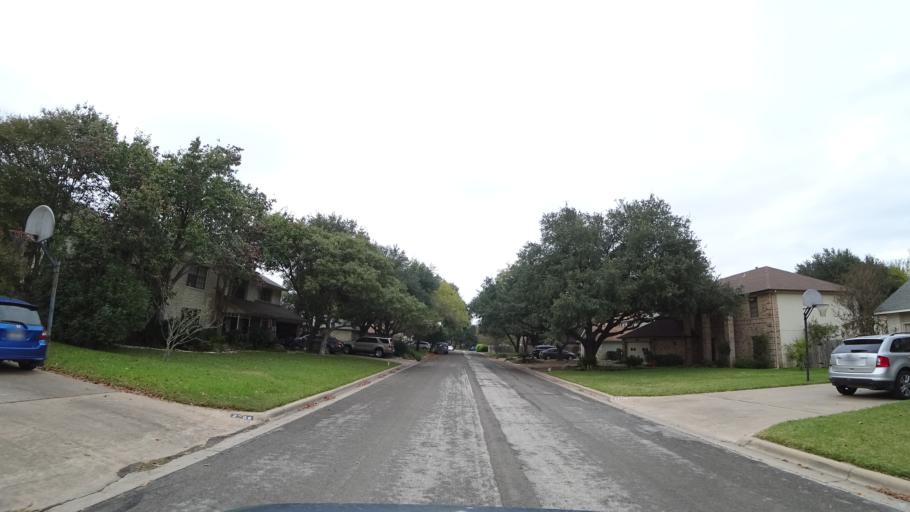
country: US
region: Texas
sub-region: Williamson County
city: Round Rock
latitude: 30.4838
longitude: -97.7045
